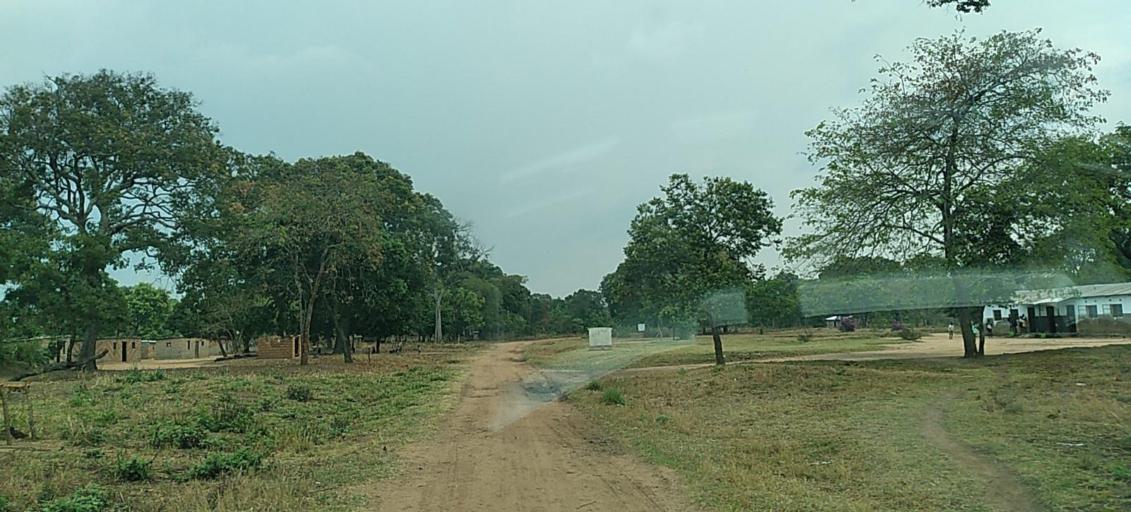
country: ZM
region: North-Western
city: Mwinilunga
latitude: -11.4517
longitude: 24.5897
